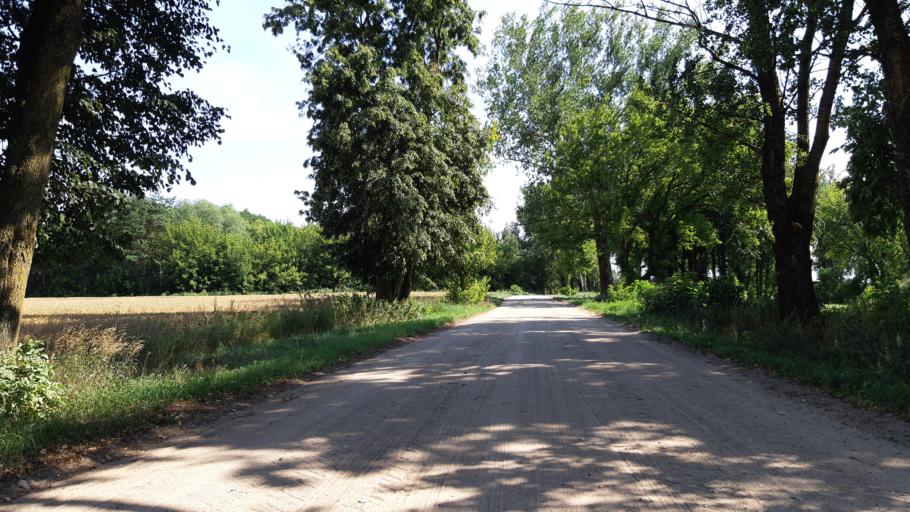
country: LT
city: Virbalis
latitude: 54.6365
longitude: 22.8244
